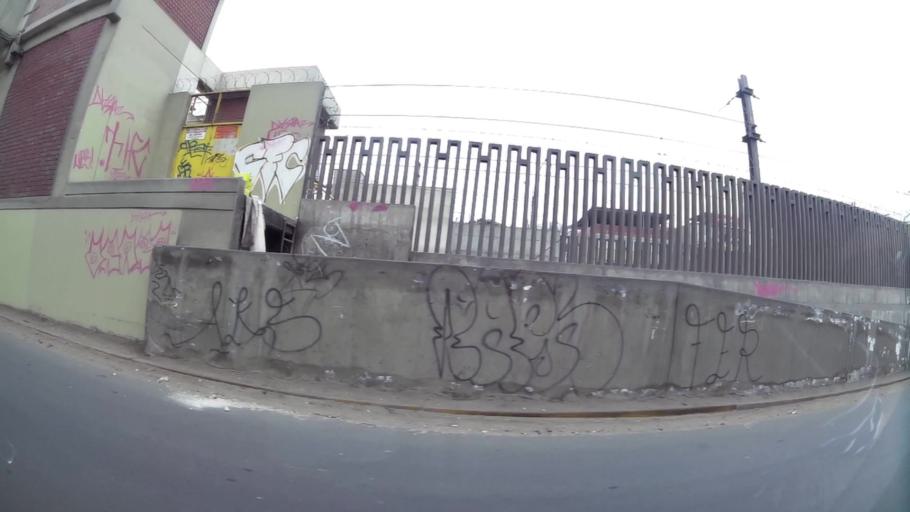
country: PE
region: Lima
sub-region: Lima
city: Surco
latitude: -12.1570
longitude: -76.9649
